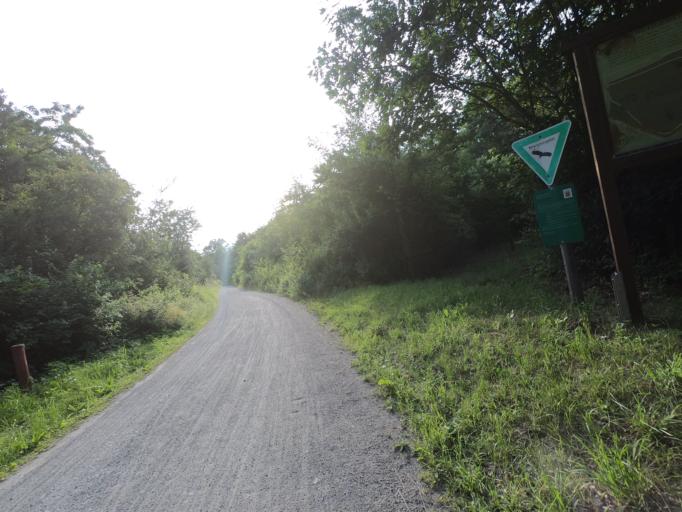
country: DE
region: Hesse
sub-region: Regierungsbezirk Darmstadt
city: Russelsheim
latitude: 49.9712
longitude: 8.4104
